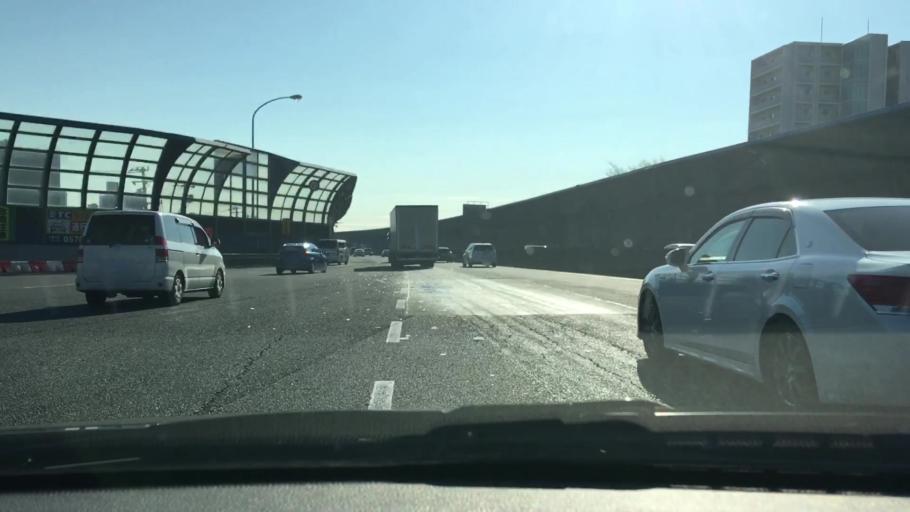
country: JP
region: Chiba
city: Funabashi
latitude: 35.6959
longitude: 139.9747
